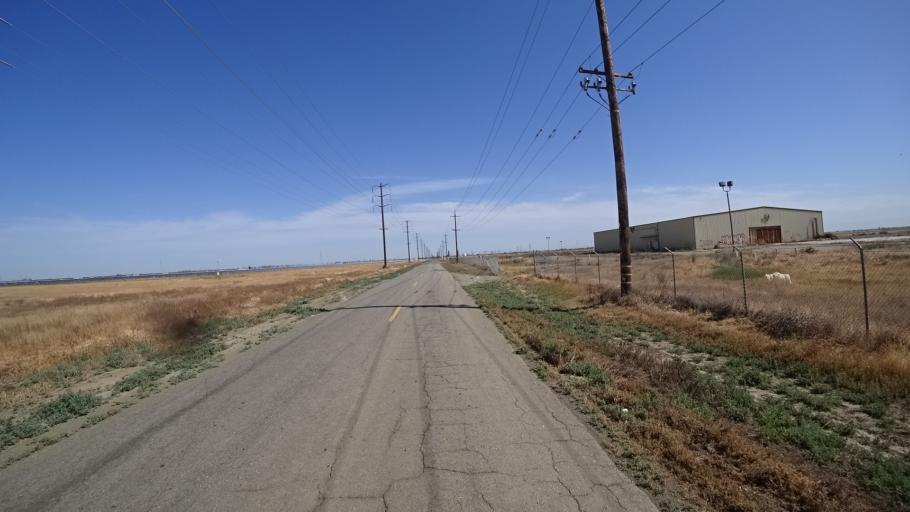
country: US
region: California
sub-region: Kings County
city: Lemoore Station
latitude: 36.2271
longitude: -119.9051
